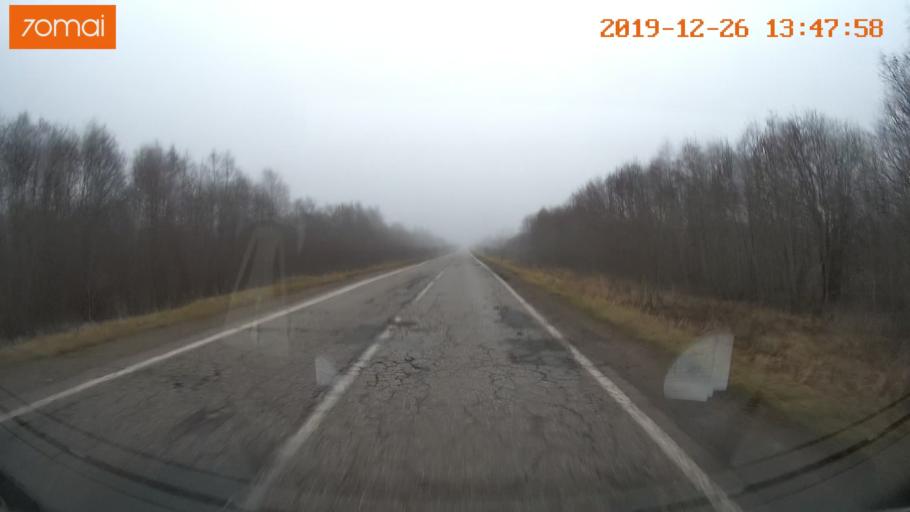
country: RU
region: Vologda
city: Sheksna
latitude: 58.6805
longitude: 38.5408
